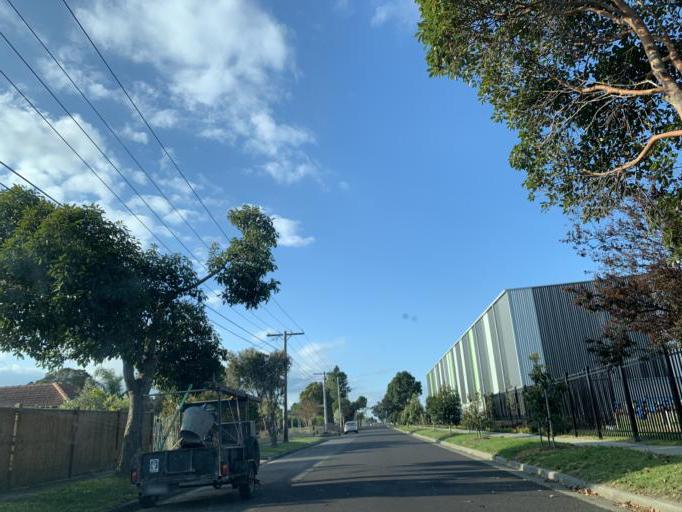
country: AU
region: Victoria
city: Heatherton
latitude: -37.9828
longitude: 145.0930
